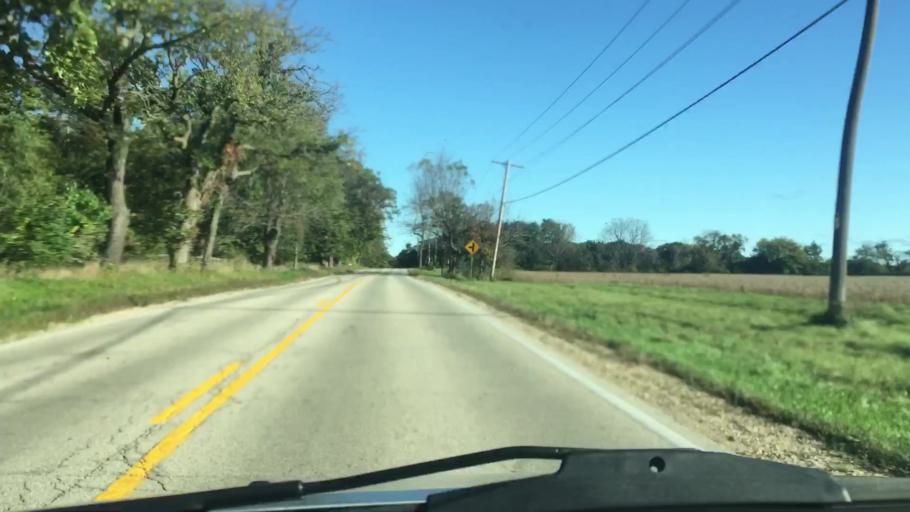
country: US
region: Wisconsin
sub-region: Waukesha County
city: North Prairie
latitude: 42.9498
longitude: -88.4053
